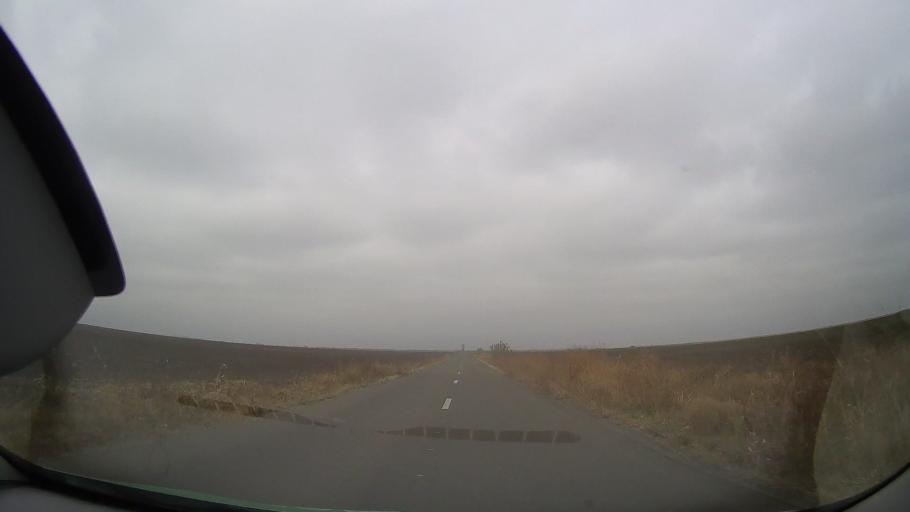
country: RO
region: Buzau
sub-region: Comuna Bradeanu
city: Bradeanu
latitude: 44.8926
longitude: 26.8739
